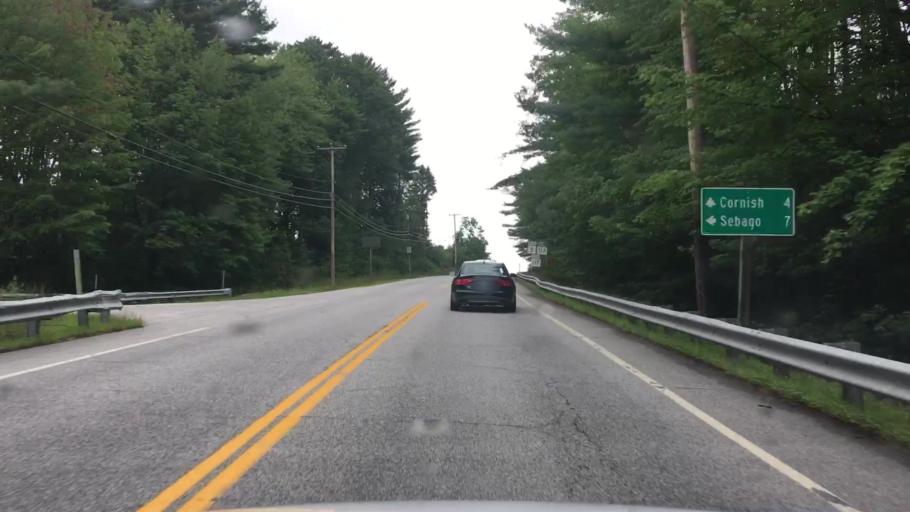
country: US
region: Maine
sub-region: York County
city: Cornish
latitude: 43.8403
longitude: -70.7811
